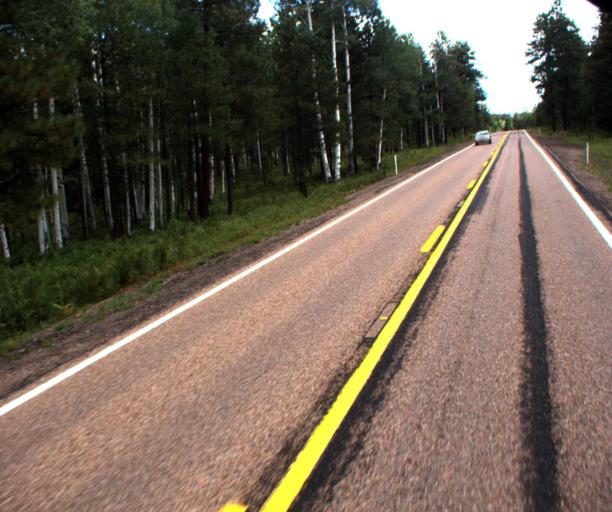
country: US
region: Arizona
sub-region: Navajo County
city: Pinetop-Lakeside
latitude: 34.0315
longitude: -109.6607
